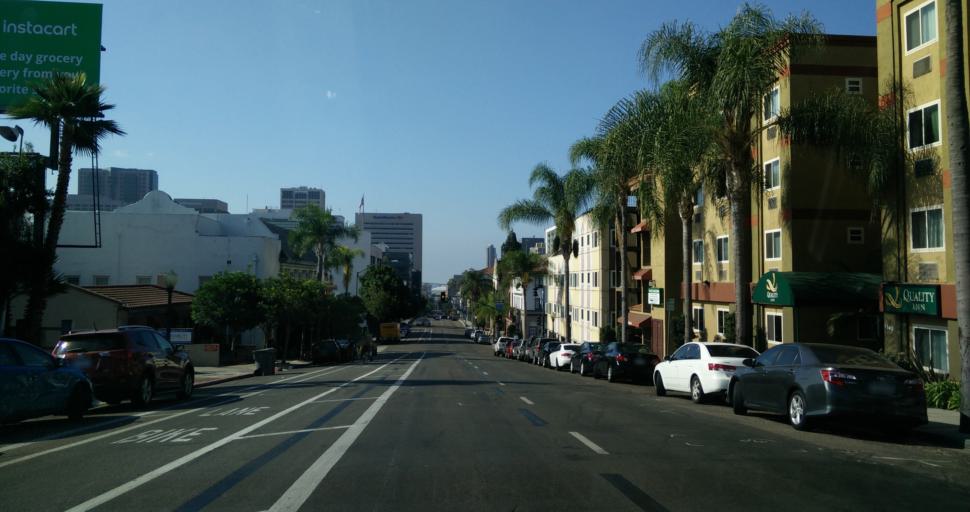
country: US
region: California
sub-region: San Diego County
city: San Diego
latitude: 32.7250
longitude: -117.1612
